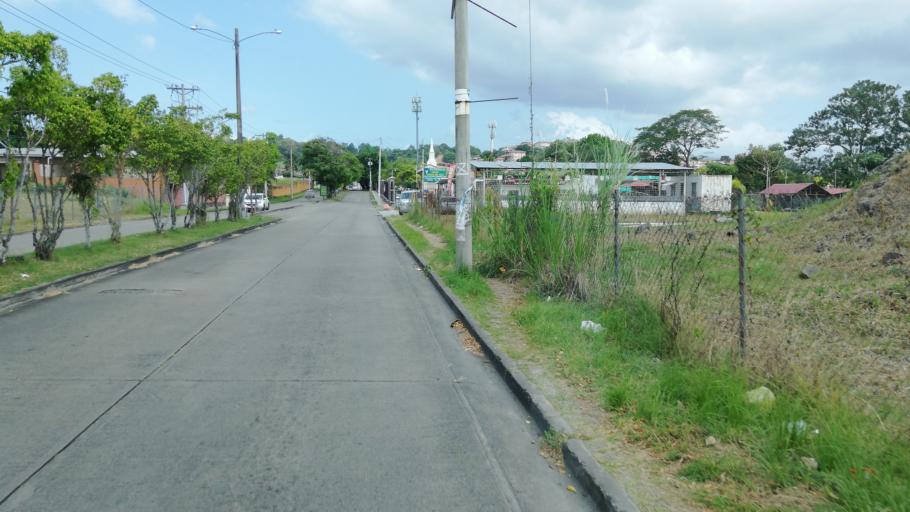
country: PA
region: Panama
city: San Miguelito
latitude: 9.0559
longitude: -79.4596
